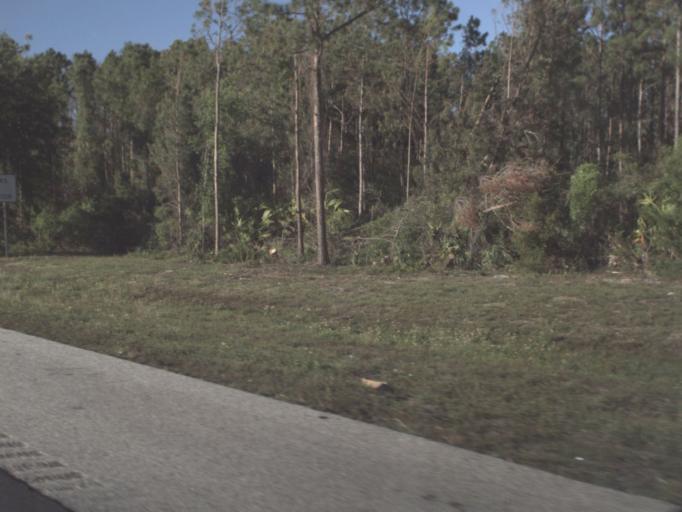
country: US
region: Florida
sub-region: Flagler County
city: Flagler Beach
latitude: 29.4932
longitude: -81.1902
